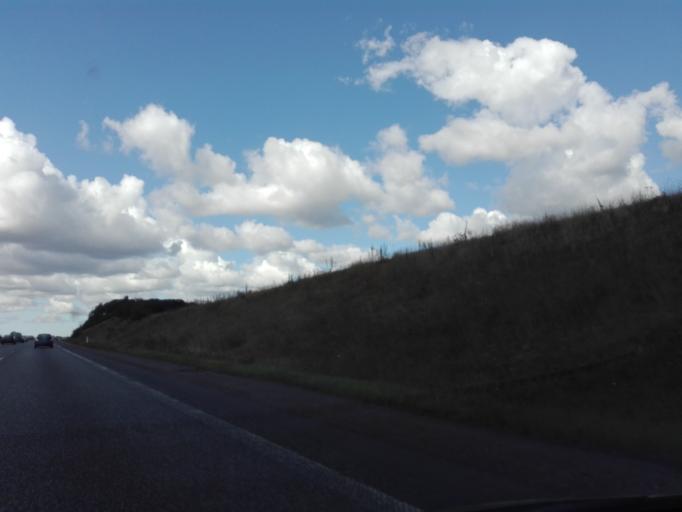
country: DK
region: North Denmark
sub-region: Mariagerfjord Kommune
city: Hobro
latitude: 56.5522
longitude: 9.8765
